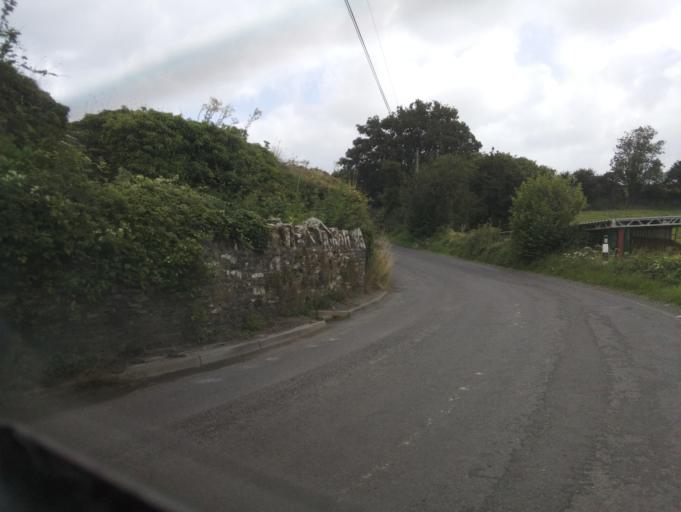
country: GB
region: England
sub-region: Dorset
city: Stalbridge
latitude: 50.9538
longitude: -2.3901
